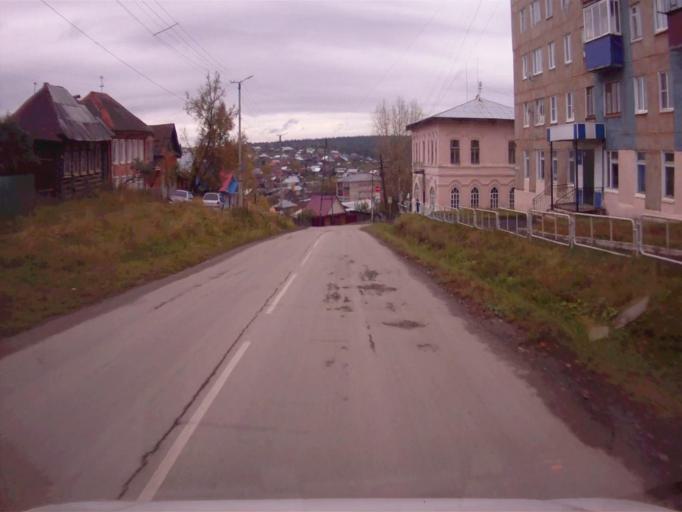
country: RU
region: Chelyabinsk
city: Nyazepetrovsk
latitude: 56.0543
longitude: 59.6036
